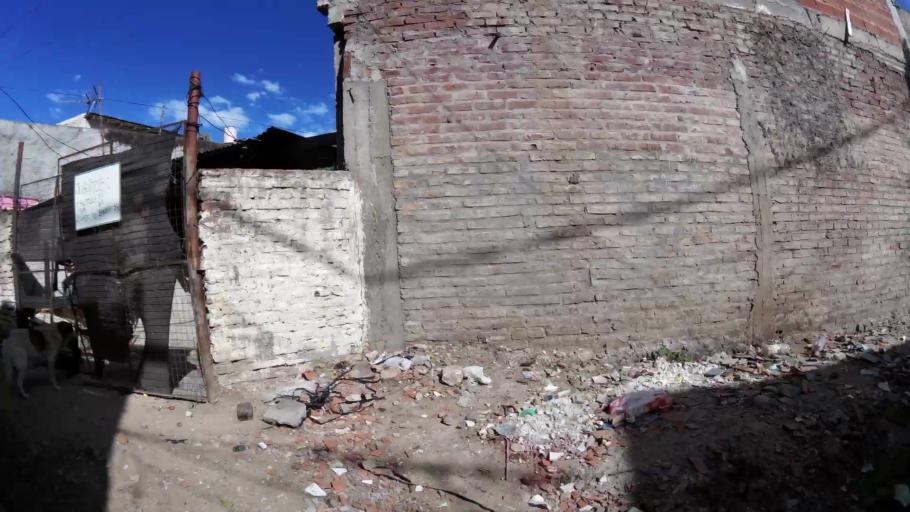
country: AR
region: Buenos Aires
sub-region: Partido de General San Martin
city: General San Martin
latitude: -34.5232
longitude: -58.5808
